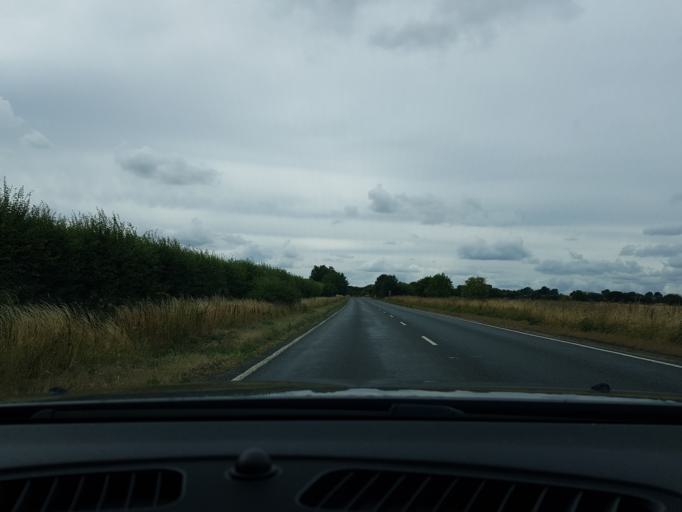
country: GB
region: England
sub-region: Hampshire
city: Tadley
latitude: 51.2892
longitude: -1.1478
